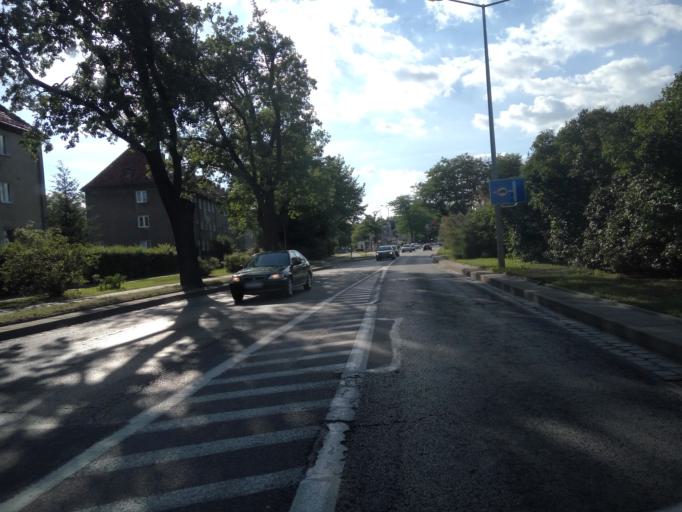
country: PL
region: Lower Silesian Voivodeship
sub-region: Powiat wroclawski
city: Wroclaw
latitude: 51.1394
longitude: 16.9609
